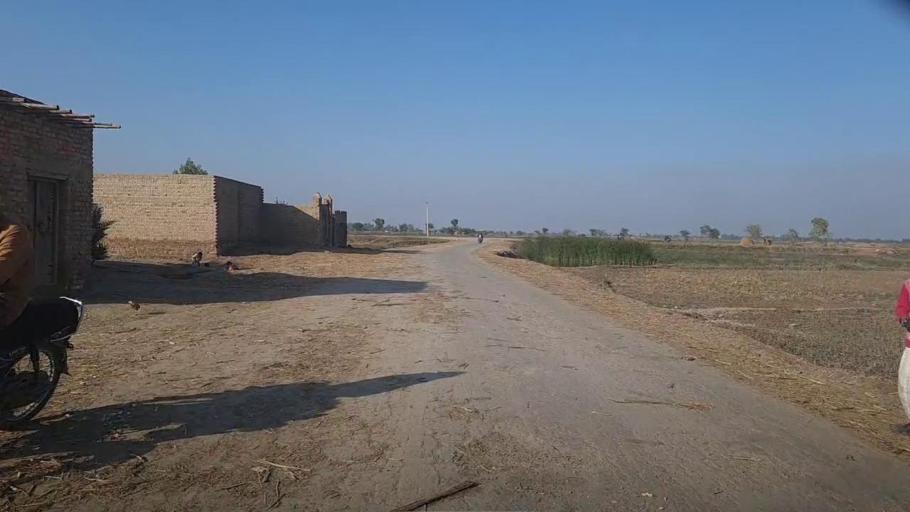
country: PK
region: Sindh
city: Phulji
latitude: 26.8681
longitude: 67.7929
